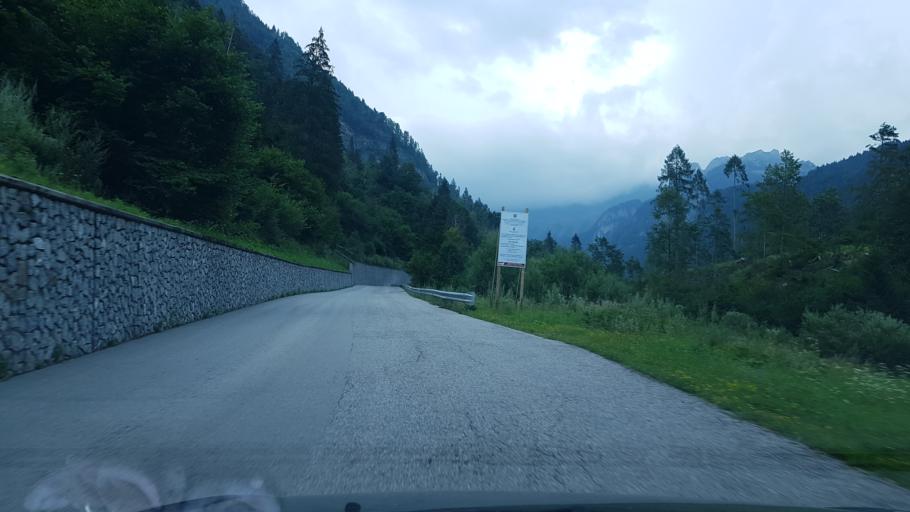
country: IT
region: Friuli Venezia Giulia
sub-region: Provincia di Udine
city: Forni Avoltri
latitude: 46.5931
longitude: 12.7751
